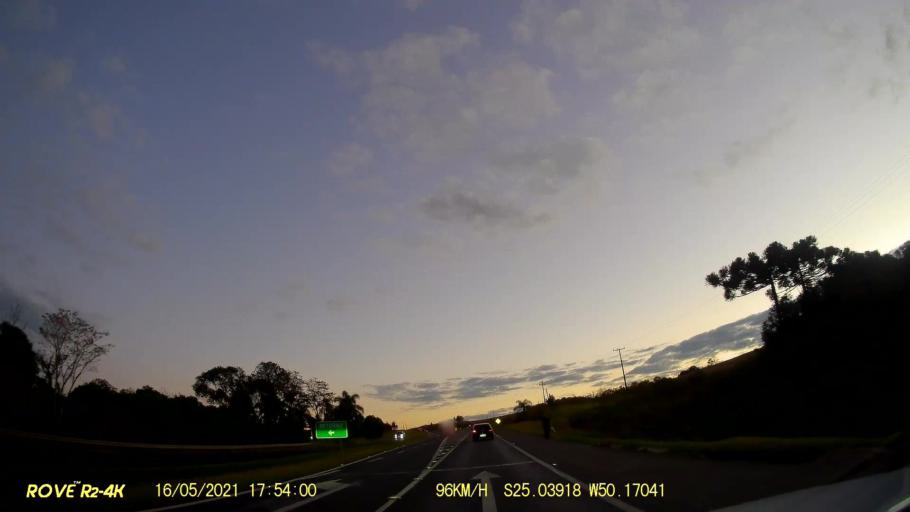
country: BR
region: Parana
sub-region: Ponta Grossa
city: Ponta Grossa
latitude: -25.0391
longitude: -50.1699
